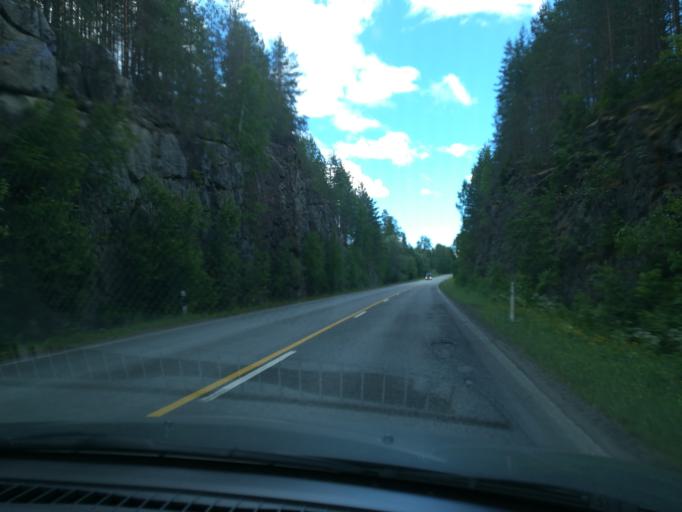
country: FI
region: Southern Savonia
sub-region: Mikkeli
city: Hirvensalmi
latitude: 61.6707
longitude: 26.8790
